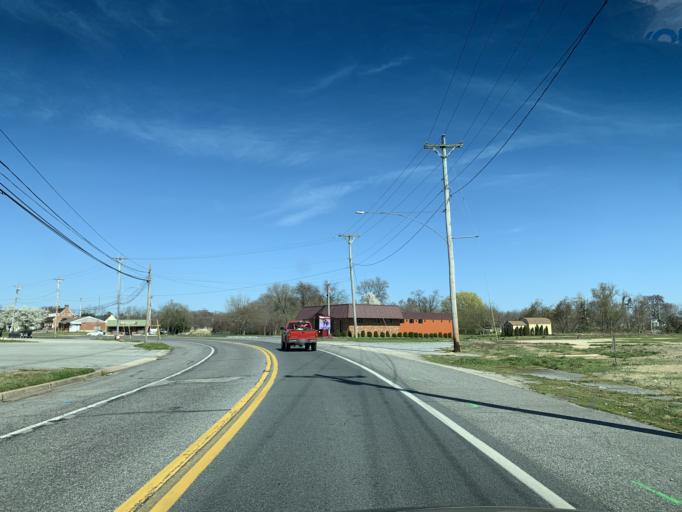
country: US
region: Delaware
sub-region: Sussex County
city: Milford
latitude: 38.9151
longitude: -75.4233
